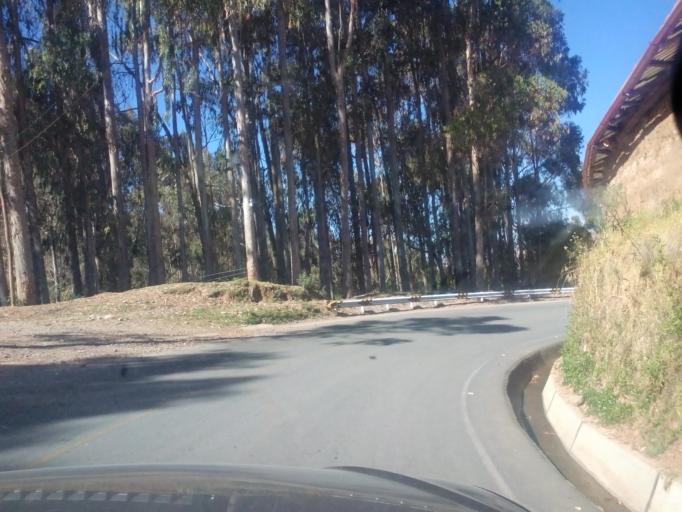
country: PE
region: Apurimac
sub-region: Provincia de Andahuaylas
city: Talavera
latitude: -13.6497
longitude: -73.5139
